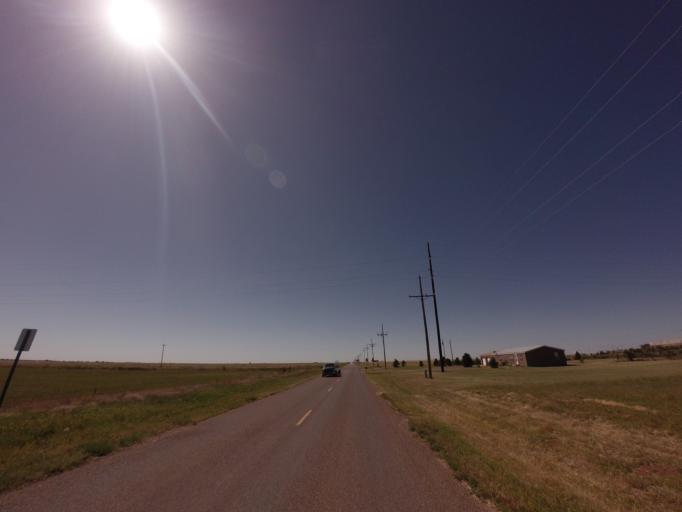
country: US
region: New Mexico
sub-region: Curry County
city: Clovis
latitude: 34.4484
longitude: -103.2129
